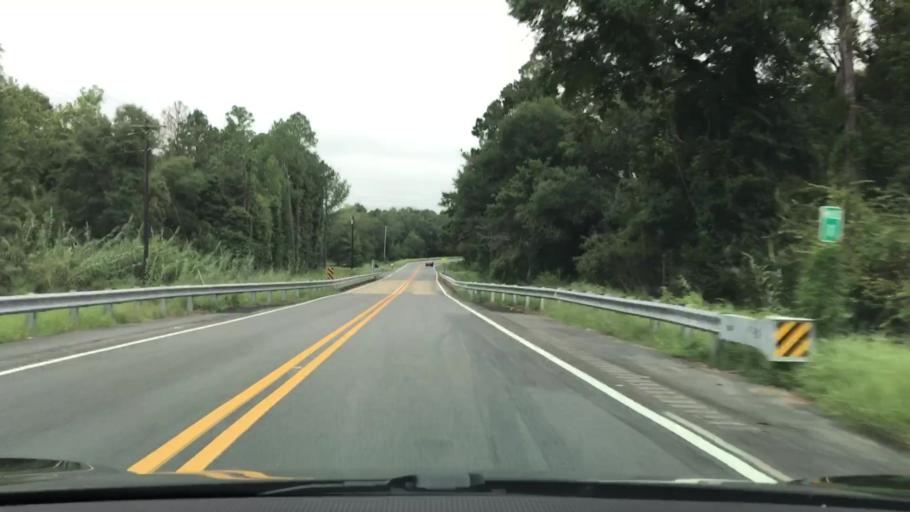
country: US
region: Alabama
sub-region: Covington County
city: Opp
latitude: 31.2251
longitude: -86.1608
